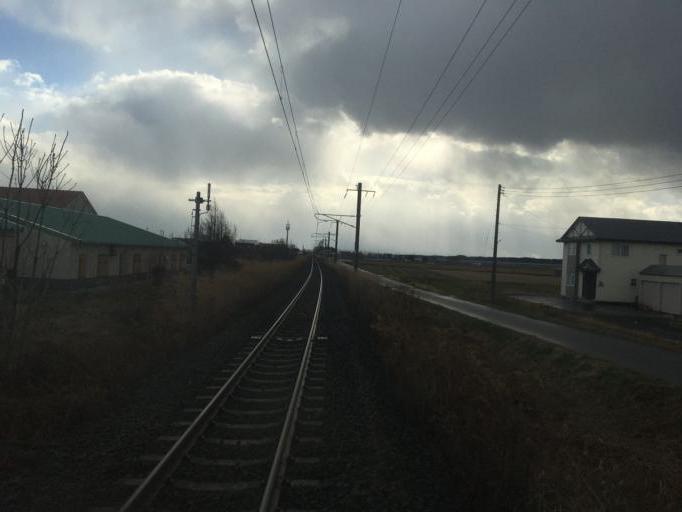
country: JP
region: Aomori
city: Aomori Shi
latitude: 40.8862
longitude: 140.6746
